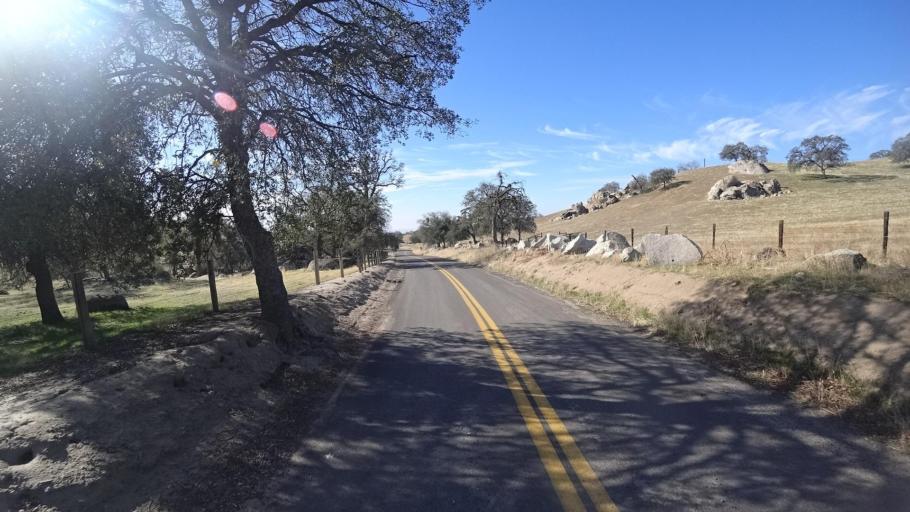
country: US
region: California
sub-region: Tulare County
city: Richgrove
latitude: 35.6780
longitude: -118.8467
